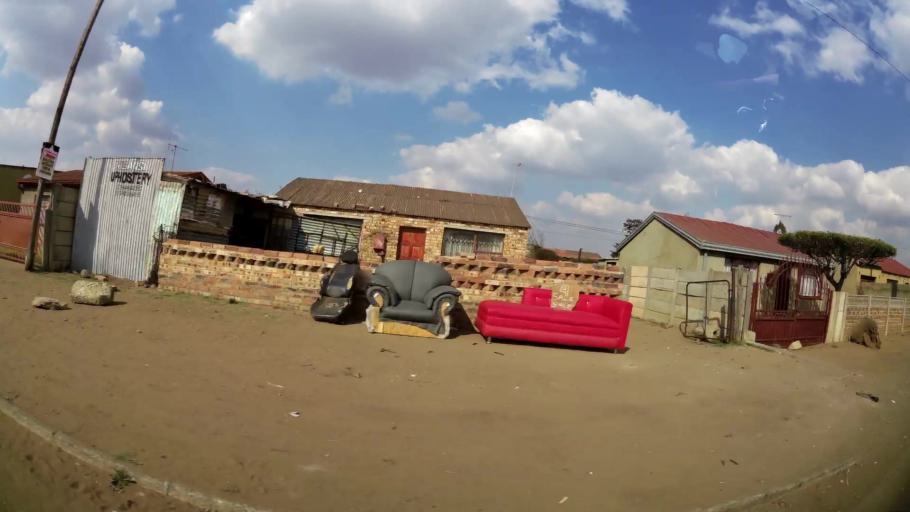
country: ZA
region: Gauteng
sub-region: Ekurhuleni Metropolitan Municipality
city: Brakpan
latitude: -26.1385
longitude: 28.4259
